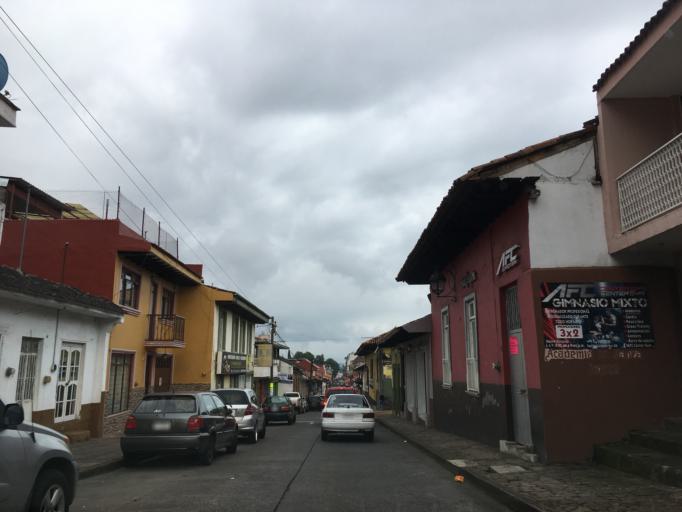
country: MX
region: Michoacan
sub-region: Uruapan
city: Uruapan
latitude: 19.4223
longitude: -102.0685
